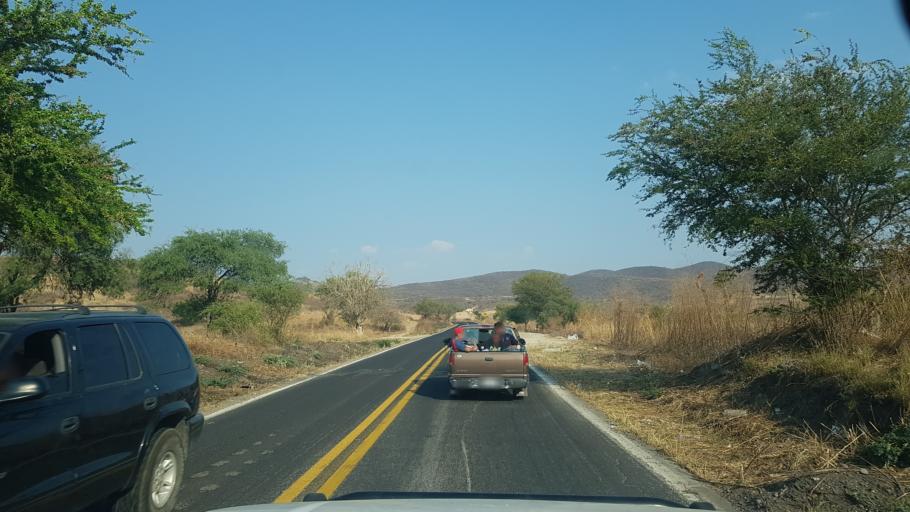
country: MX
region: Puebla
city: Calmeca
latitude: 18.6428
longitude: -98.6216
